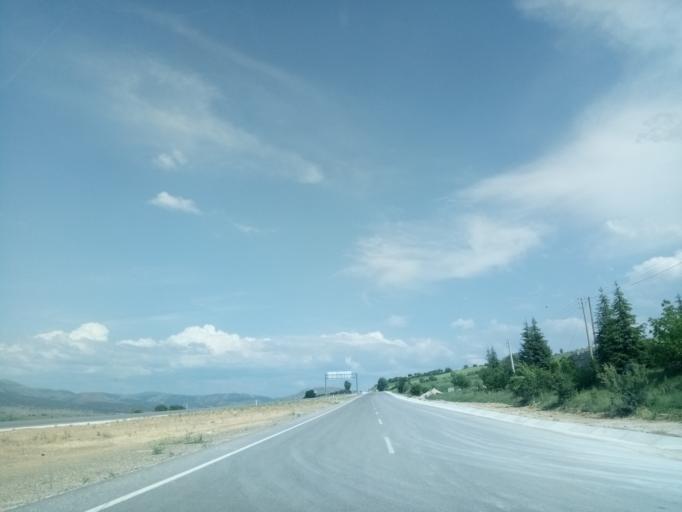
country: TR
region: Isparta
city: Bagkonak
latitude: 38.1765
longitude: 31.2608
